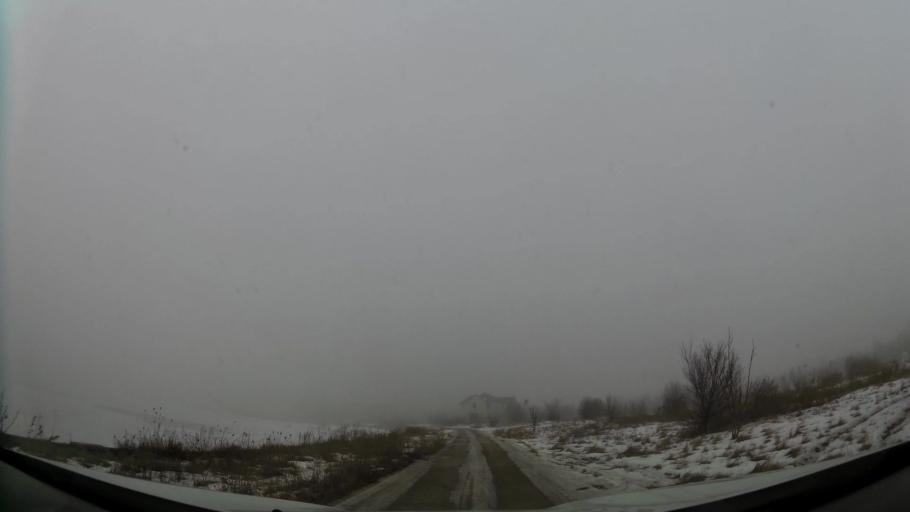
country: RO
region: Ilfov
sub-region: Comuna Chiajna
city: Rosu
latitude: 44.4496
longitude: 26.0278
